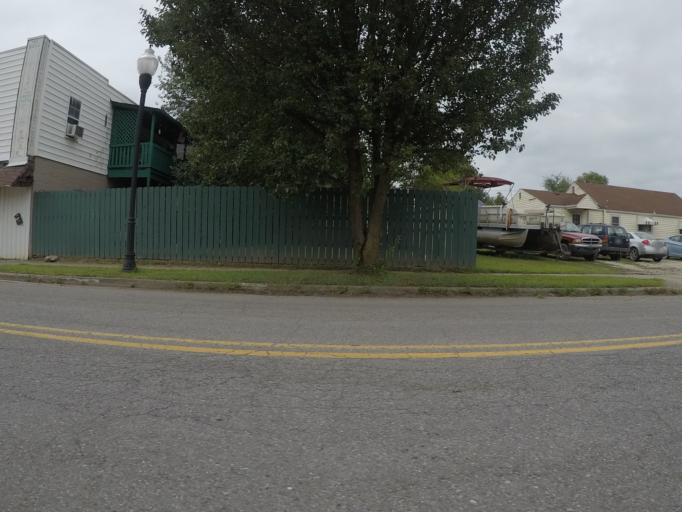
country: US
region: West Virginia
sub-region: Cabell County
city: Huntington
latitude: 38.4276
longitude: -82.3868
